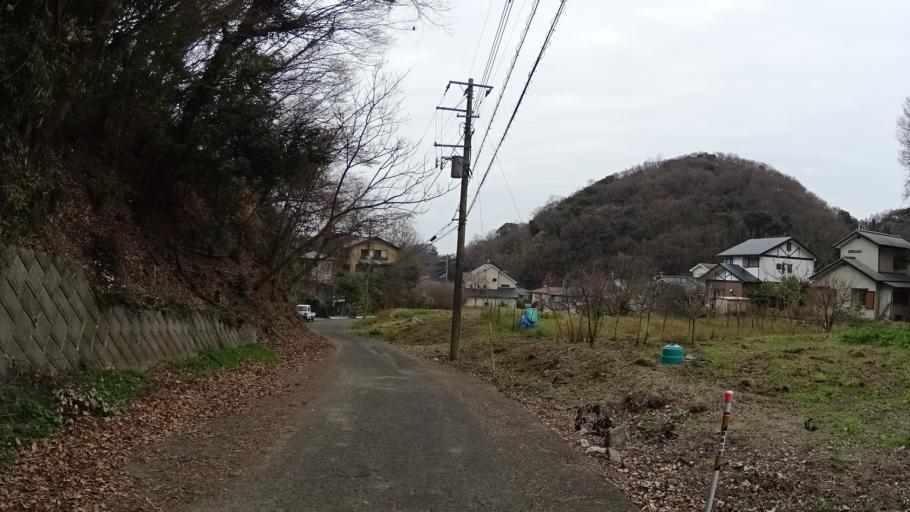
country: JP
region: Kanagawa
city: Oiso
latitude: 35.3165
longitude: 139.3081
